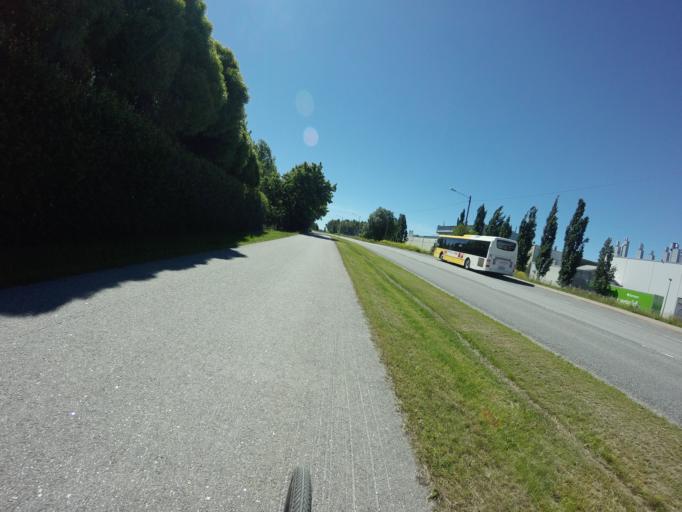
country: FI
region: Varsinais-Suomi
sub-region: Turku
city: Turku
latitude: 60.4797
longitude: 22.2978
